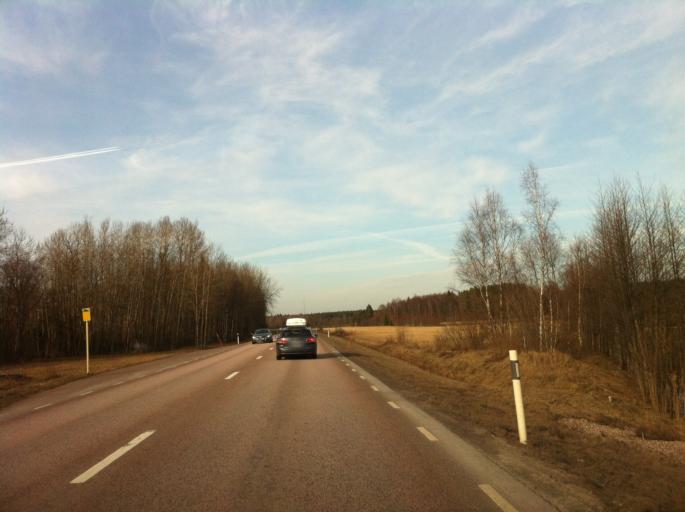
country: SE
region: Vaermland
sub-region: Kristinehamns Kommun
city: Bjorneborg
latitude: 59.2111
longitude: 14.1834
